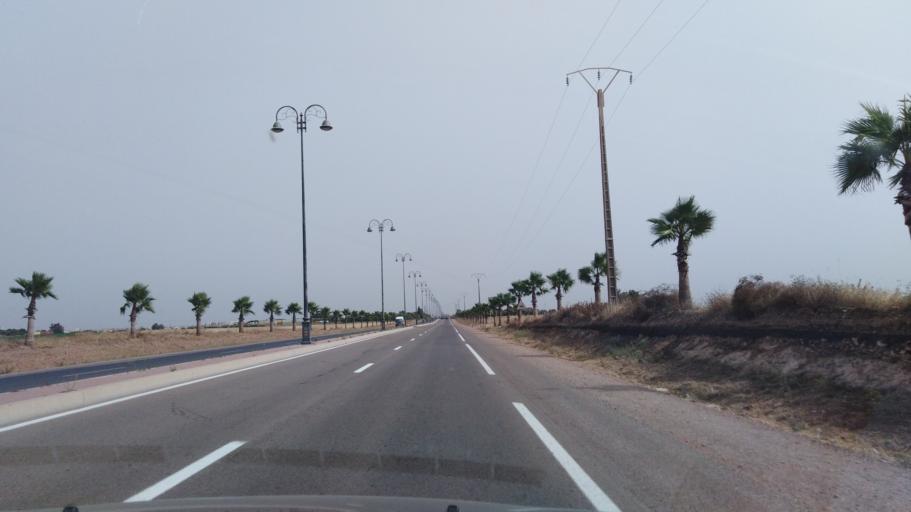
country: MA
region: Chaouia-Ouardigha
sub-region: Settat Province
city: Berrechid
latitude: 33.2960
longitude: -7.5969
